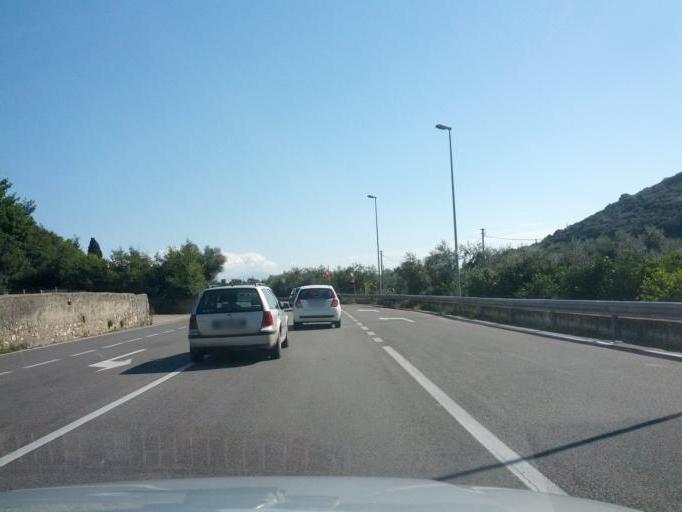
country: IT
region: Latium
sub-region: Provincia di Latina
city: Gaeta
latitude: 41.2543
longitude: 13.5655
